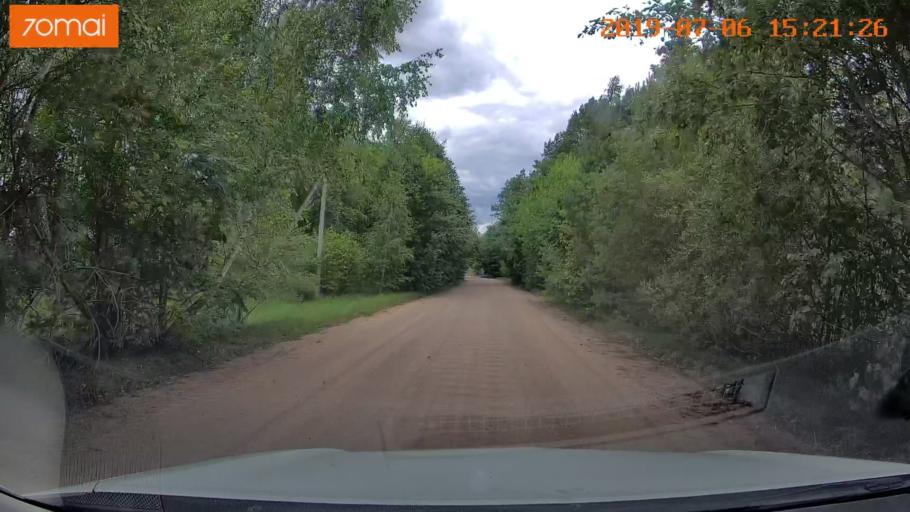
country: BY
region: Minsk
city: Valozhyn
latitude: 54.0106
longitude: 26.6145
